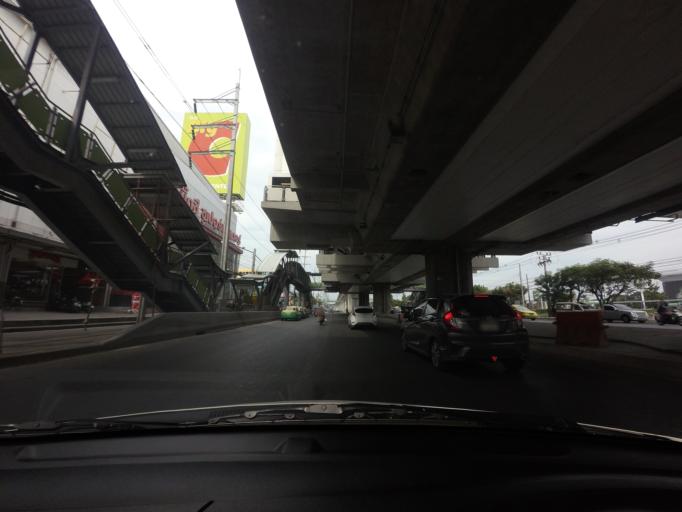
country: TH
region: Samut Prakan
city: Samut Prakan
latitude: 13.5841
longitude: 100.6077
